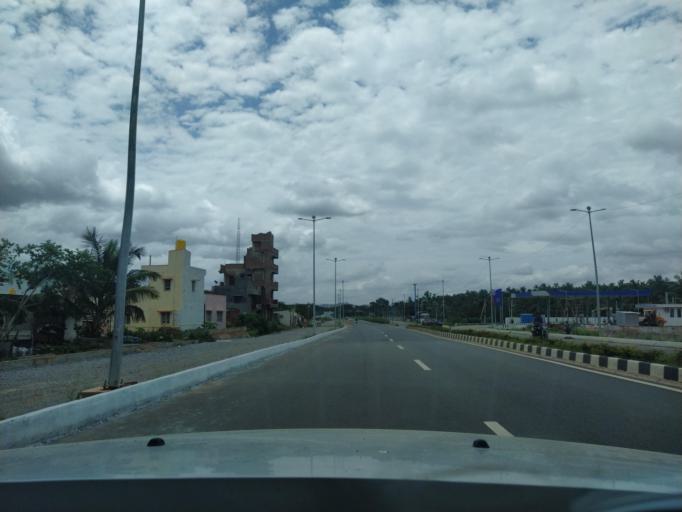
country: IN
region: Karnataka
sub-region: Tumkur
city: Tumkur
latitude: 13.3083
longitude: 77.1468
